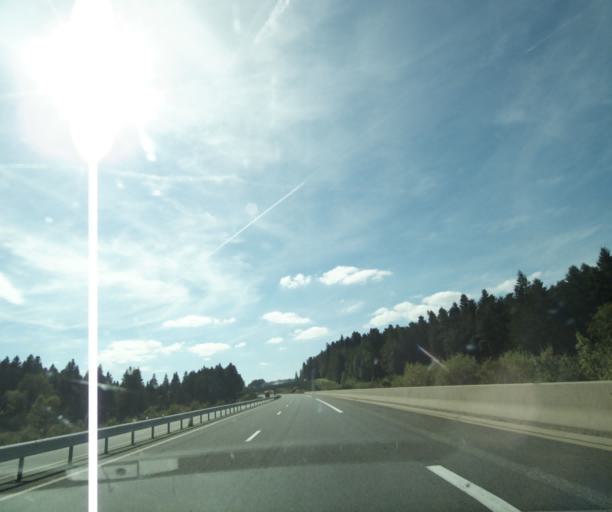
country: FR
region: Auvergne
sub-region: Departement du Puy-de-Dome
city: Gelles
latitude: 45.7496
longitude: 2.7172
